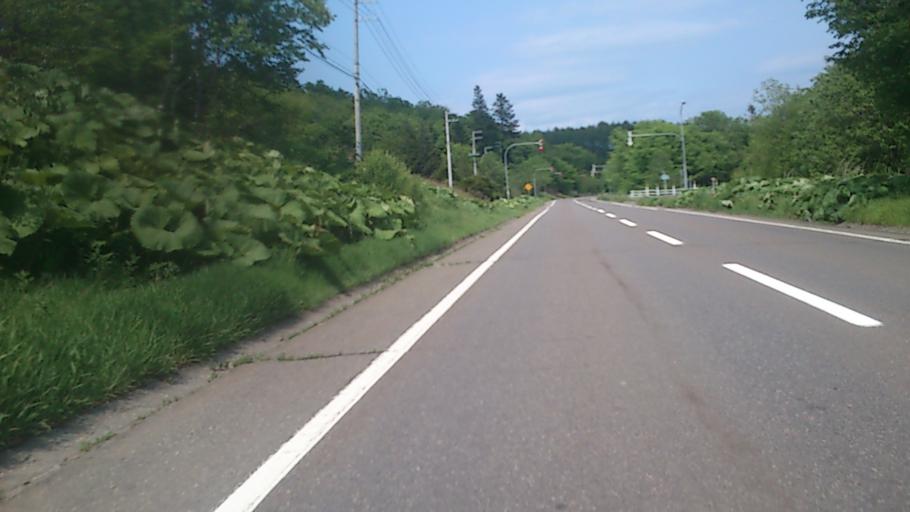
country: JP
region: Hokkaido
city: Otofuke
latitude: 43.2829
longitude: 143.6276
